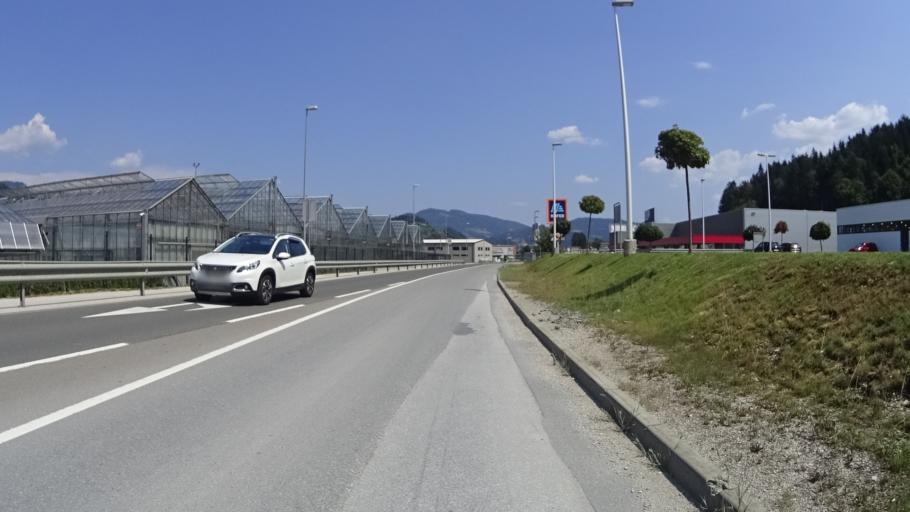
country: SI
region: Prevalje
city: Prevalje
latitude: 46.5453
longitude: 14.9352
